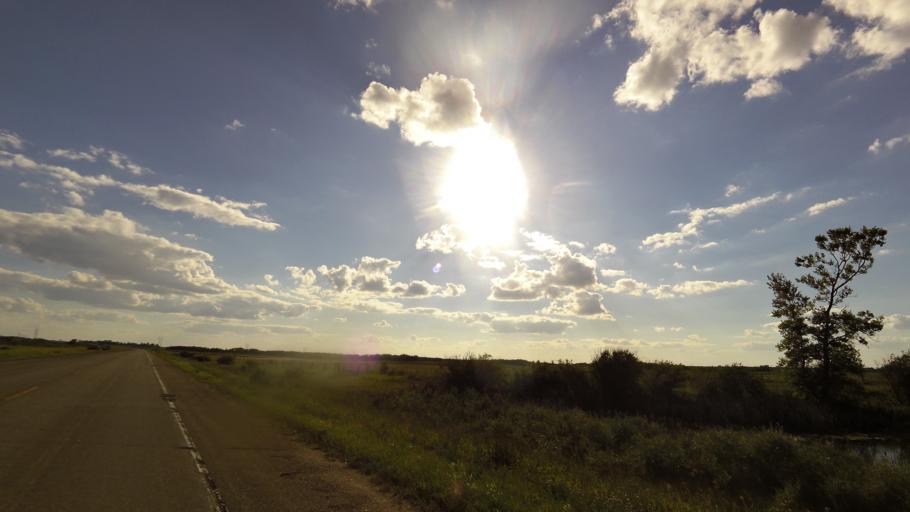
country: CA
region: Saskatchewan
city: Lanigan
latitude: 51.8667
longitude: -105.2077
